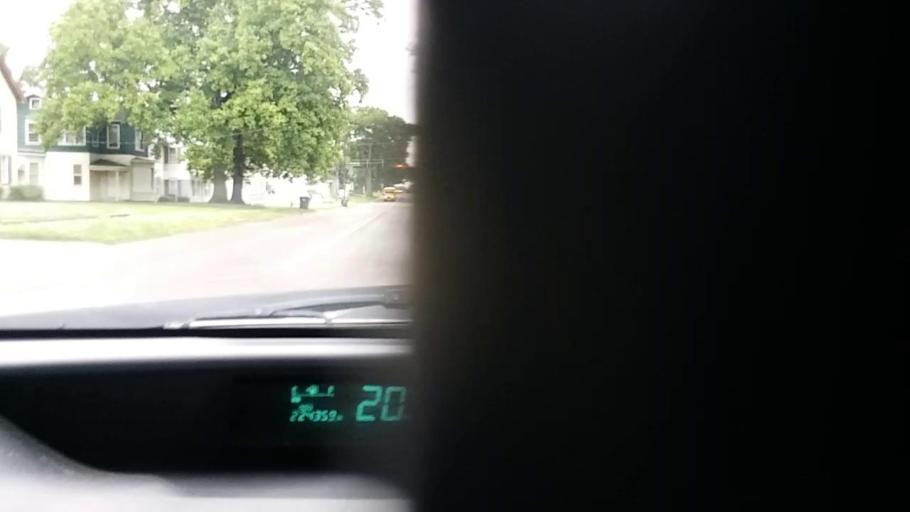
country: US
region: Illinois
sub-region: Peoria County
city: Peoria
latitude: 40.7020
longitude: -89.6036
